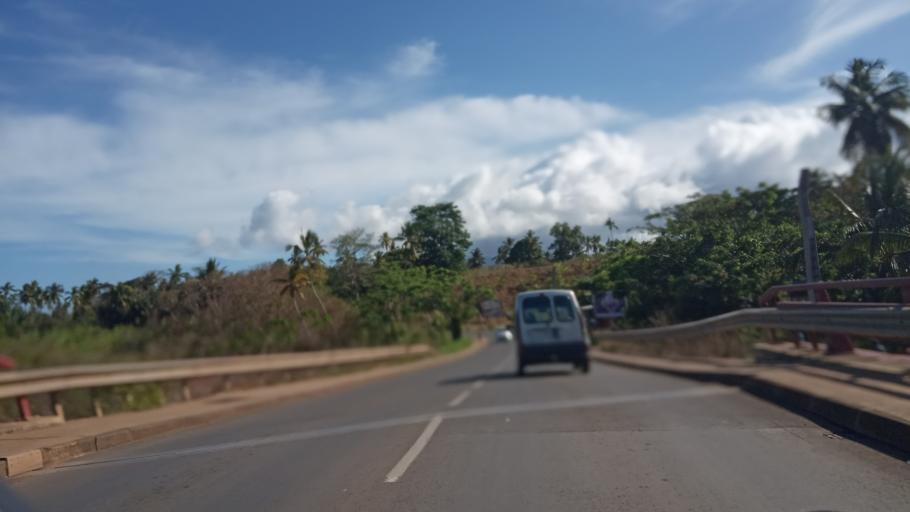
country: YT
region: Mamoudzou
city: Mamoudzou
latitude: -12.8097
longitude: 45.2032
